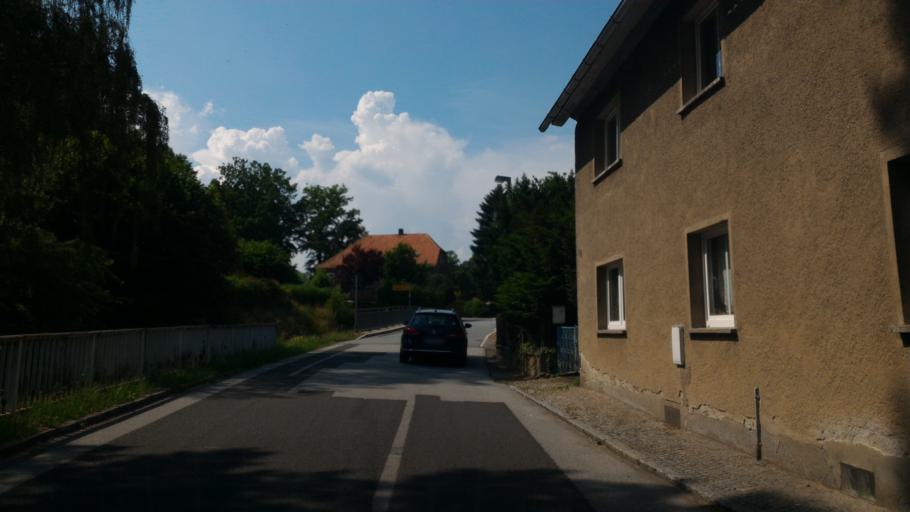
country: DE
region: Saxony
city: Hirschfelde
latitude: 50.9421
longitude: 14.8391
